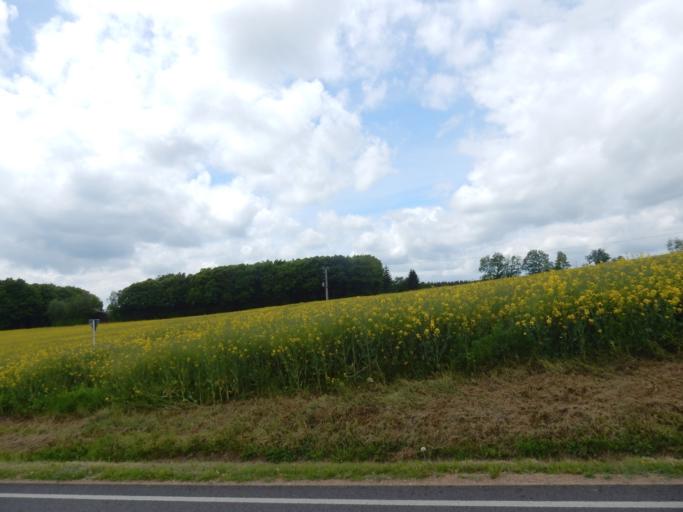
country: LU
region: Diekirch
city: Warken
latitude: 49.8711
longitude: 6.0958
